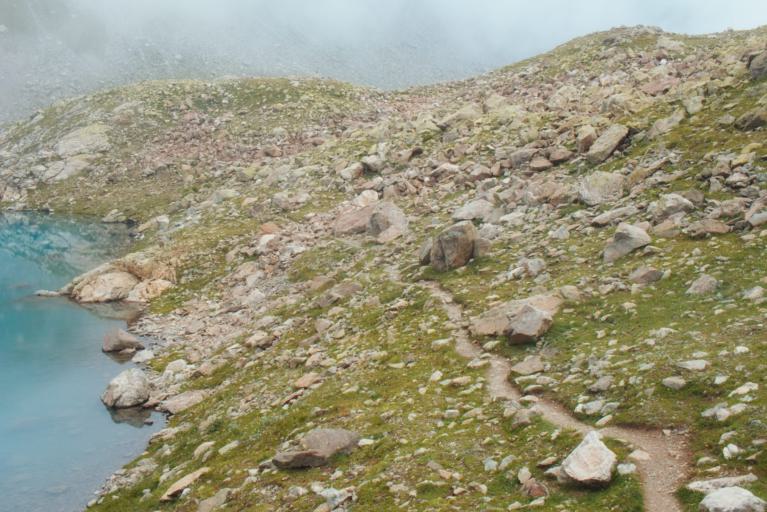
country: RU
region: Karachayevo-Cherkesiya
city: Nizhniy Arkhyz
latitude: 43.4502
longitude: 41.2329
